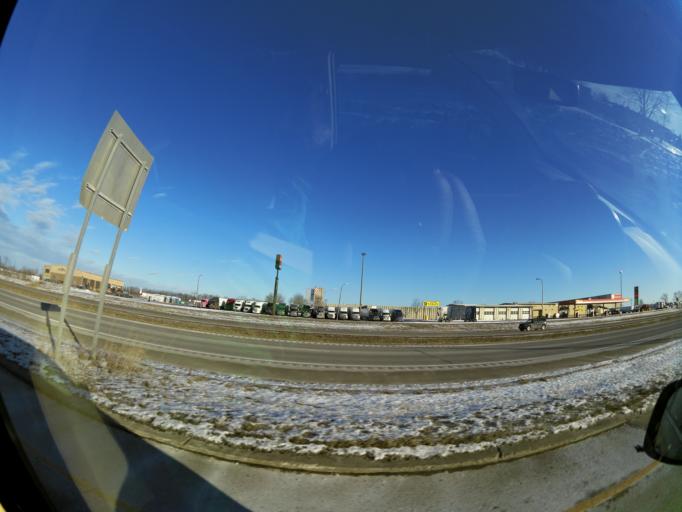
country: US
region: Minnesota
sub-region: Dakota County
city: Inver Grove Heights
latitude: 44.7817
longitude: -93.0351
